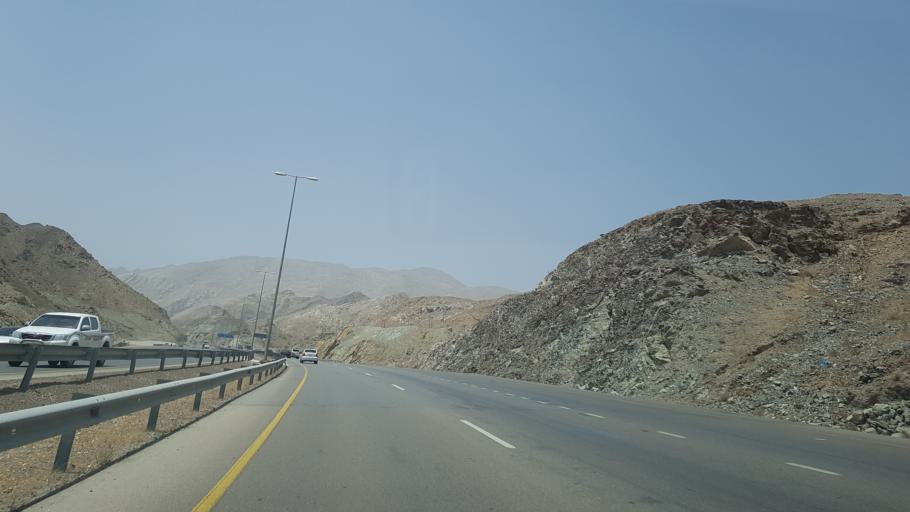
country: OM
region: Muhafazat ad Dakhiliyah
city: Bidbid
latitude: 23.4140
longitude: 58.0992
